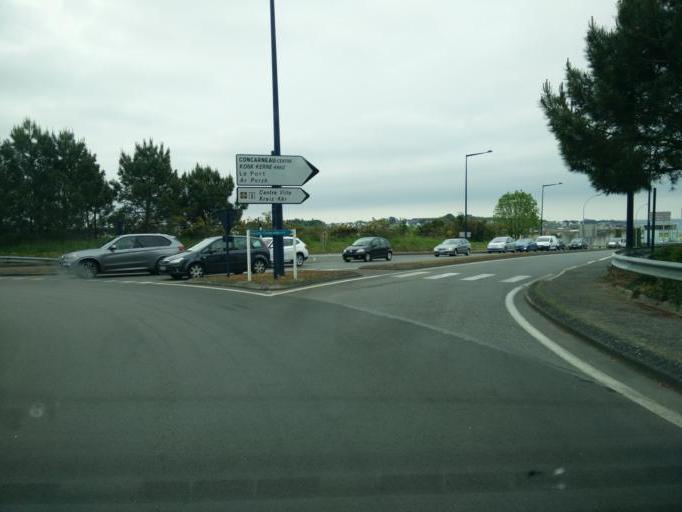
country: FR
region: Brittany
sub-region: Departement du Finistere
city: Concarneau
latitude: 47.8796
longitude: -3.9066
